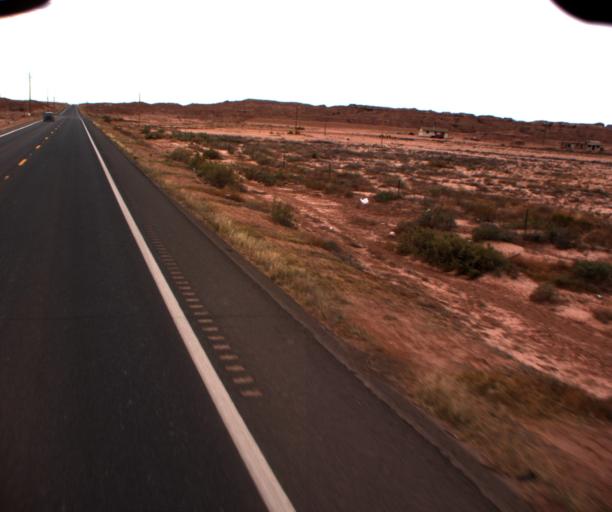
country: US
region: Arizona
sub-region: Coconino County
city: Tuba City
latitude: 36.1045
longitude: -111.2744
